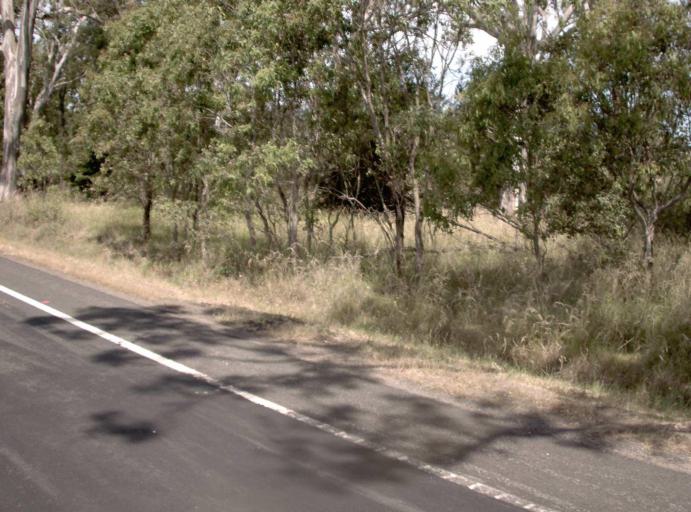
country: AU
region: Victoria
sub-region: Wellington
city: Sale
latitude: -37.9280
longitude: 147.2114
